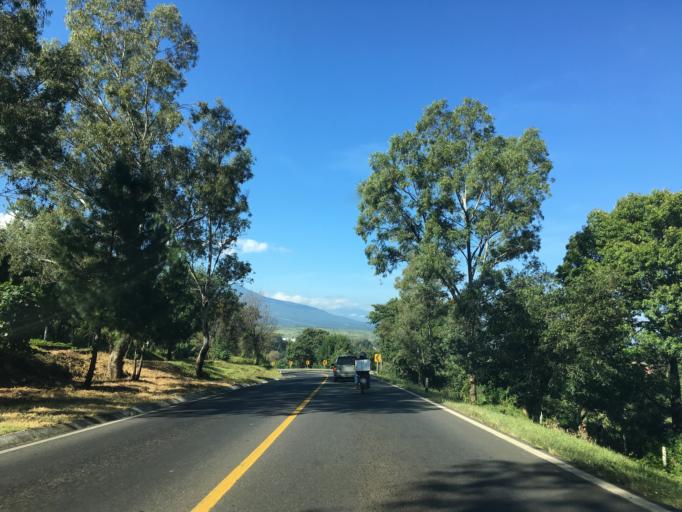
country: MX
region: Michoacan
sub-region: Chilchota
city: Ichan
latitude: 19.8478
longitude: -102.0610
